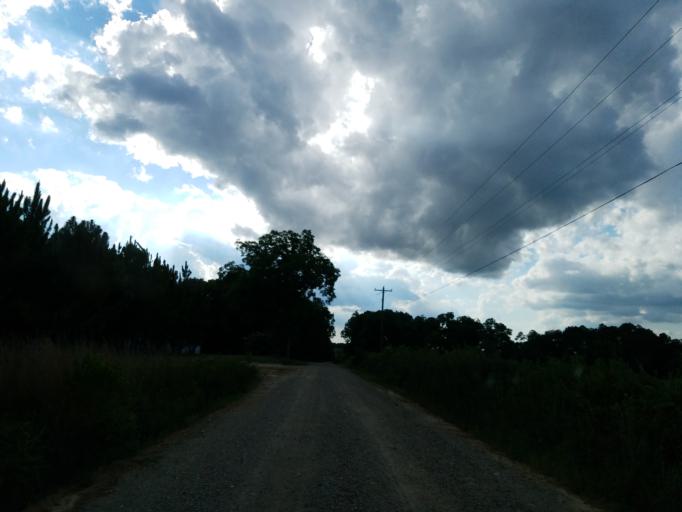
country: US
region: Georgia
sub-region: Turner County
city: Ashburn
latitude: 31.7461
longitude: -83.6650
